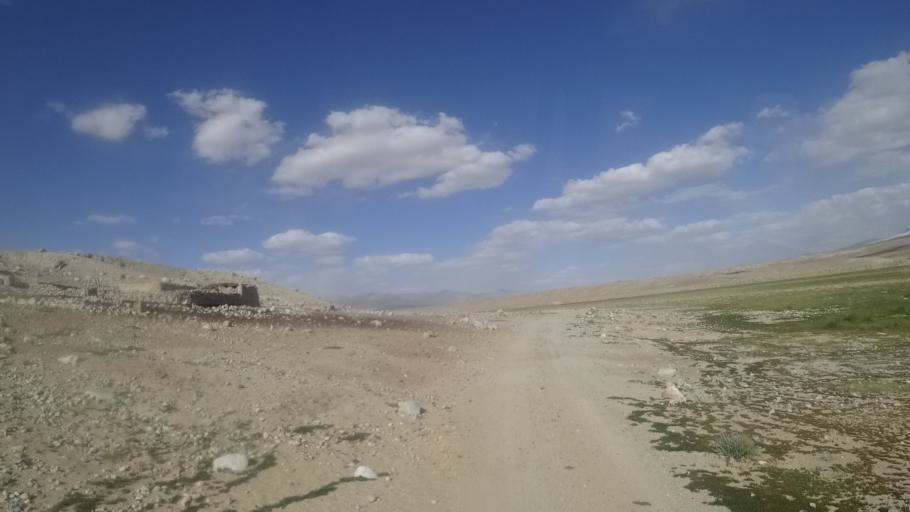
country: AF
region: Badakhshan
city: Khandud
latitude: 37.4167
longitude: 73.2296
